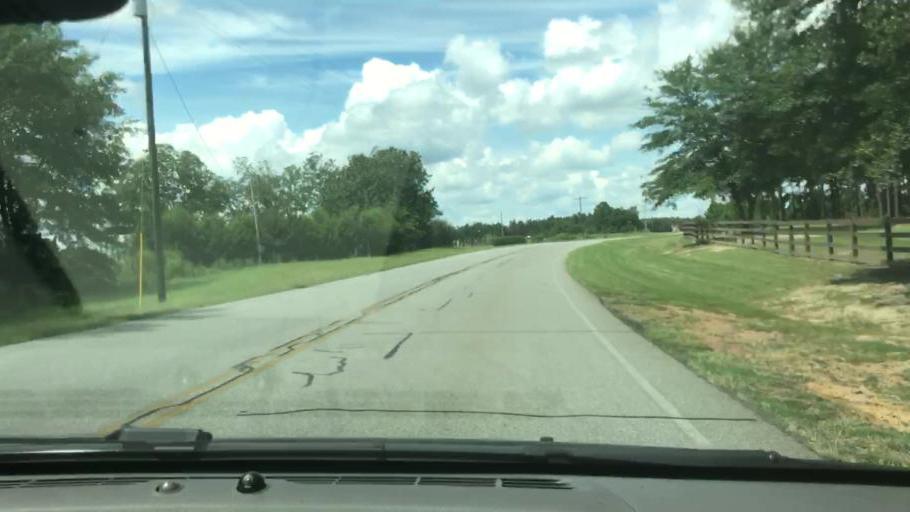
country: US
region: Georgia
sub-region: Stewart County
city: Lumpkin
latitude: 32.1372
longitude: -85.0008
